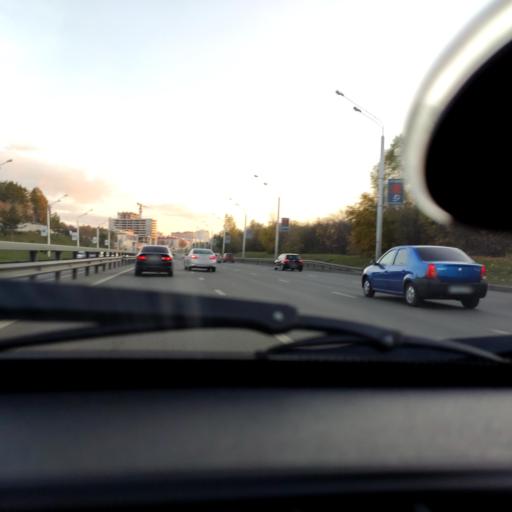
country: RU
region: Bashkortostan
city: Ufa
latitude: 54.7443
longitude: 56.0119
